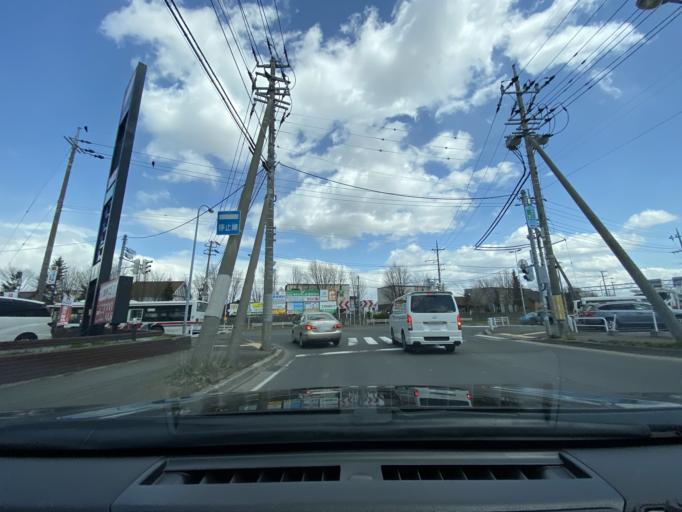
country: JP
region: Hokkaido
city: Kitahiroshima
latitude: 42.9796
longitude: 141.4848
